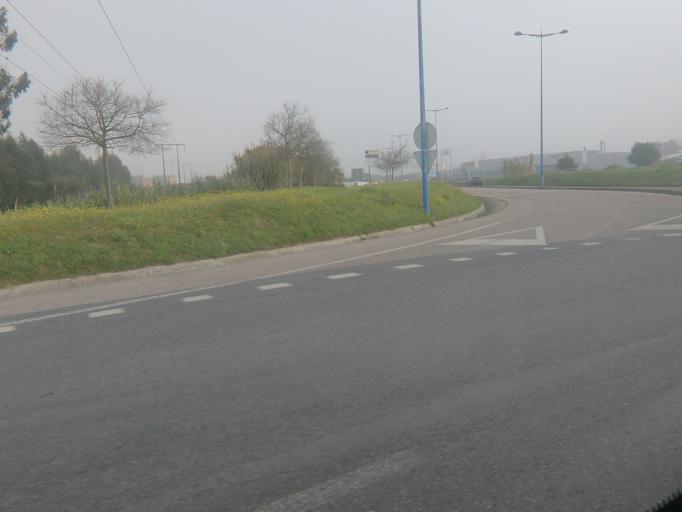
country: PT
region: Setubal
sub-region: Montijo
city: Montijo
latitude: 38.6935
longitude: -8.9507
